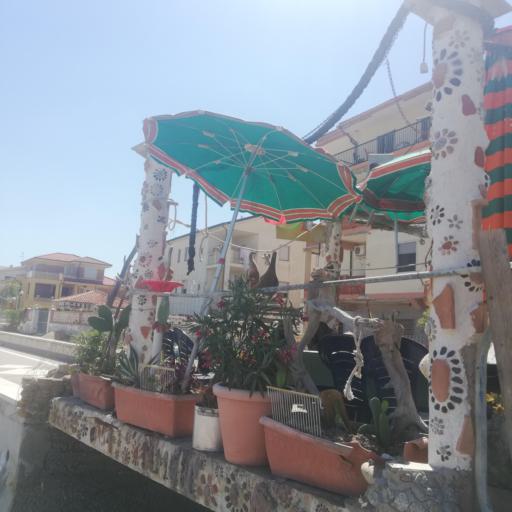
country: IT
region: Calabria
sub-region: Provincia di Cosenza
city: Caloppezzati
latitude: 39.5482
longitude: 16.8524
